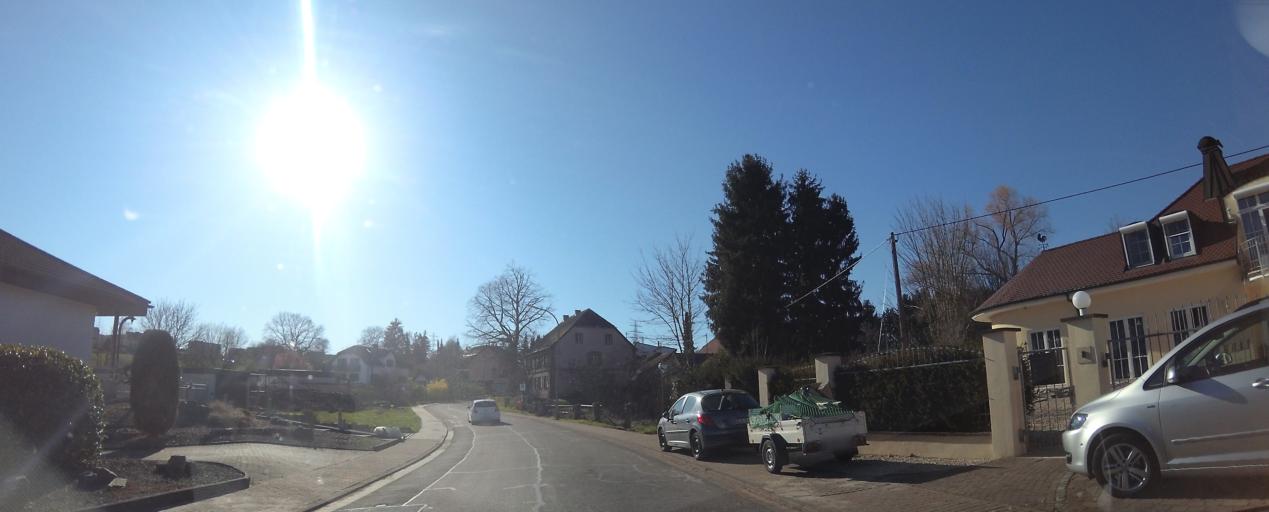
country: DE
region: Saarland
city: Riegelsberg
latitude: 49.3201
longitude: 6.9459
